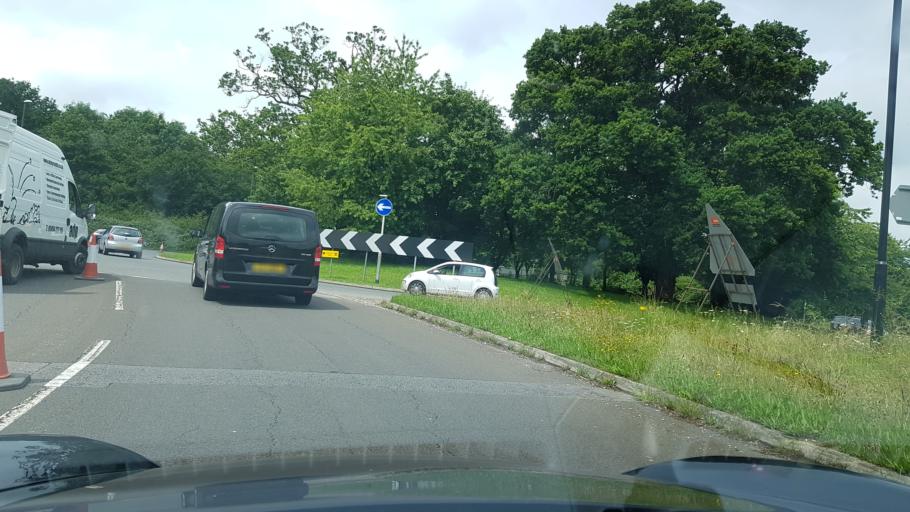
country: GB
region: England
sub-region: West Sussex
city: Horsham
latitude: 51.0876
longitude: -0.3038
